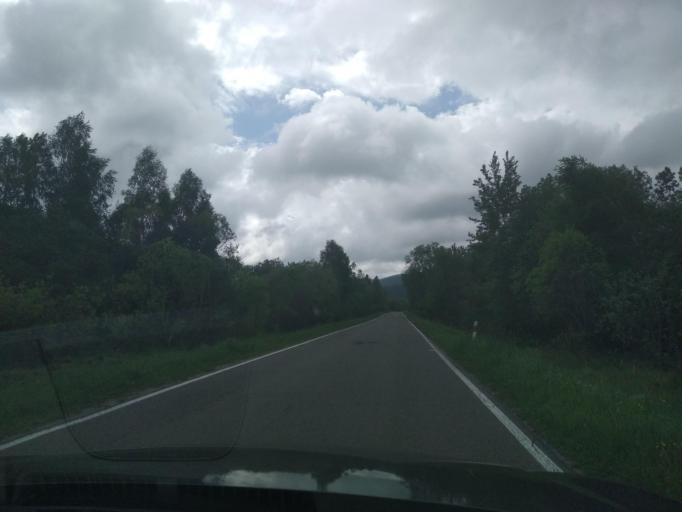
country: PL
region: Subcarpathian Voivodeship
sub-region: Powiat bieszczadzki
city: Lutowiska
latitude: 49.0911
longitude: 22.6487
